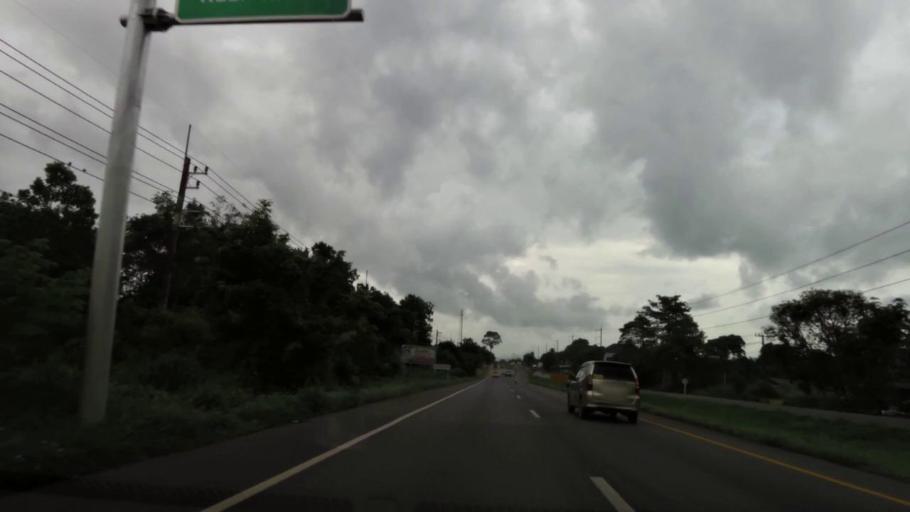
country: TH
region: Chanthaburi
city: Tha Mai
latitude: 12.6863
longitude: 102.0008
